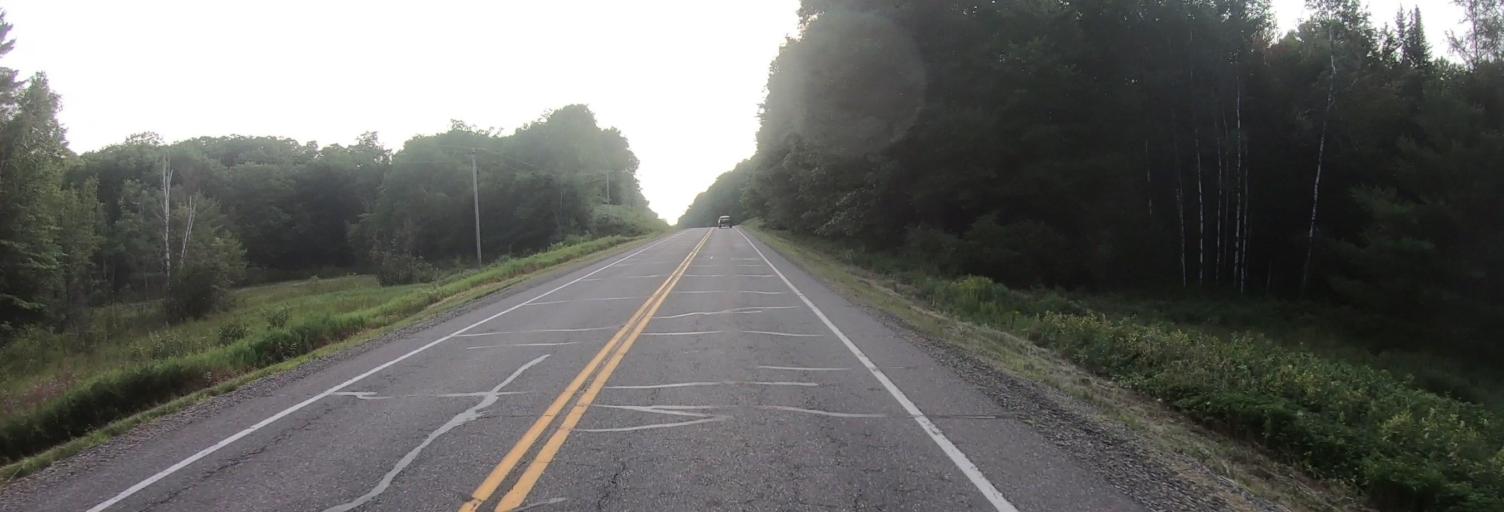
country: US
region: Wisconsin
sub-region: Sawyer County
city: Little Round Lake
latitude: 46.0655
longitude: -91.1360
